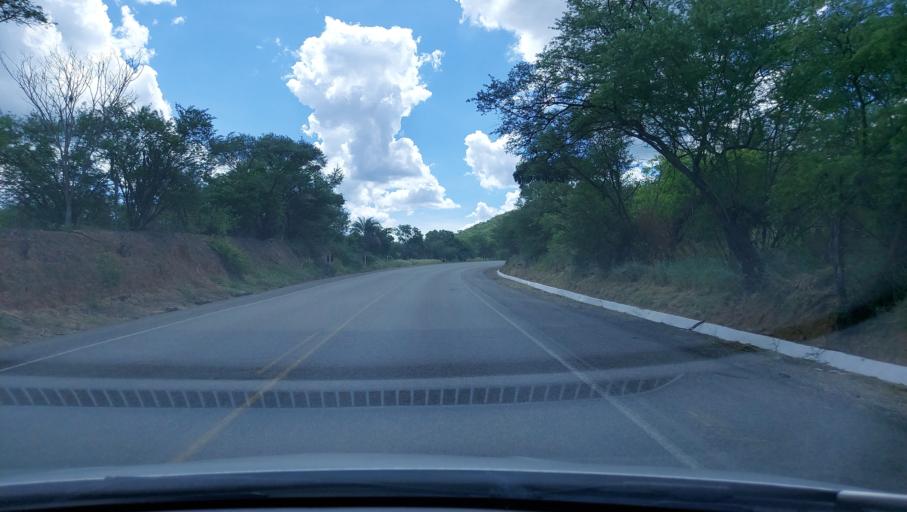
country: BR
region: Bahia
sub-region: Itaberaba
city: Itaberaba
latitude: -12.5110
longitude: -40.4899
